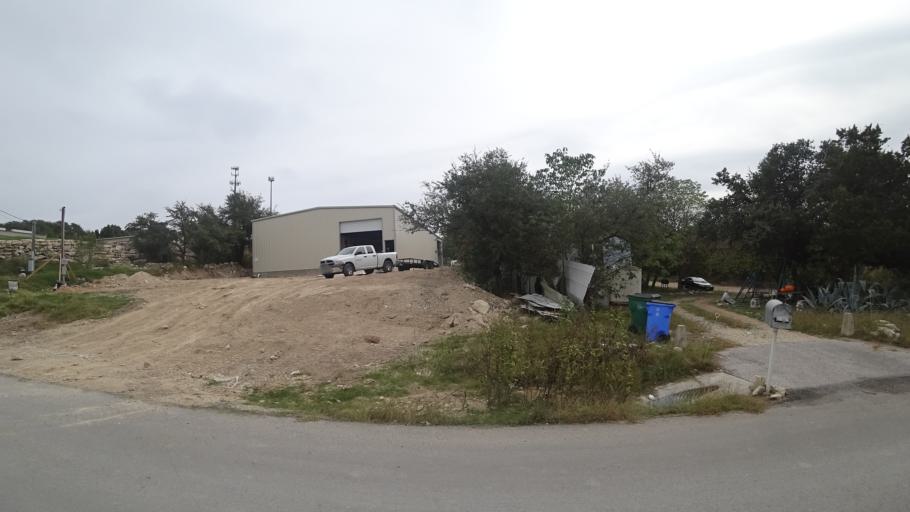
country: US
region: Texas
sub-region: Travis County
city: Hudson Bend
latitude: 30.3957
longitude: -97.9280
